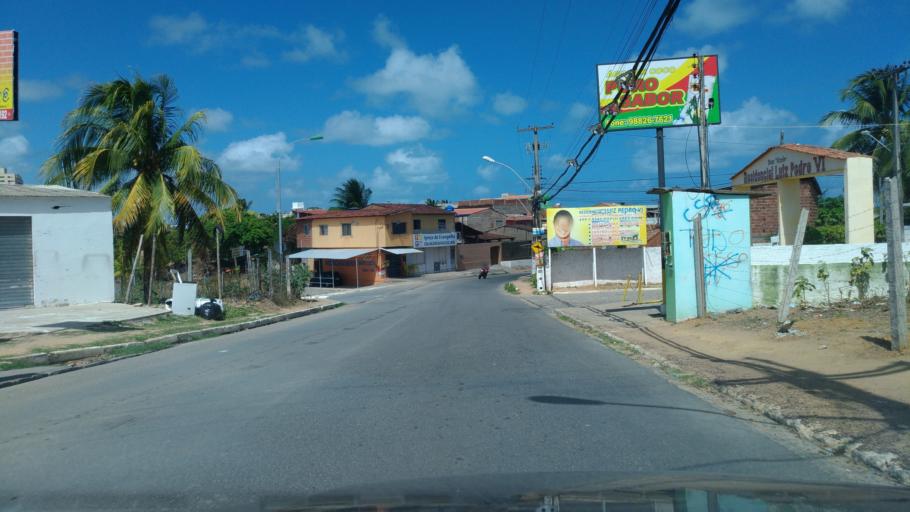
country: BR
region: Alagoas
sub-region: Maceio
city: Maceio
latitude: -9.6172
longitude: -35.7041
